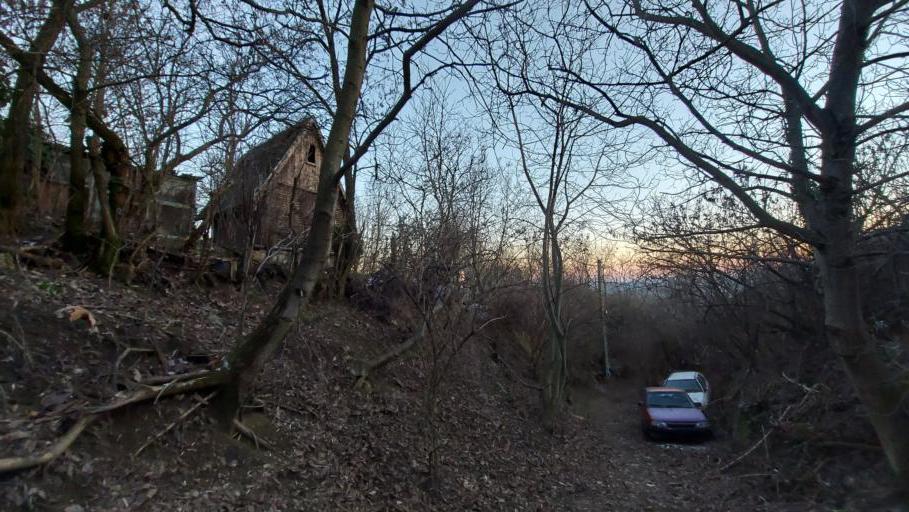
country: HU
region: Pest
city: Budaors
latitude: 47.4736
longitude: 18.9556
